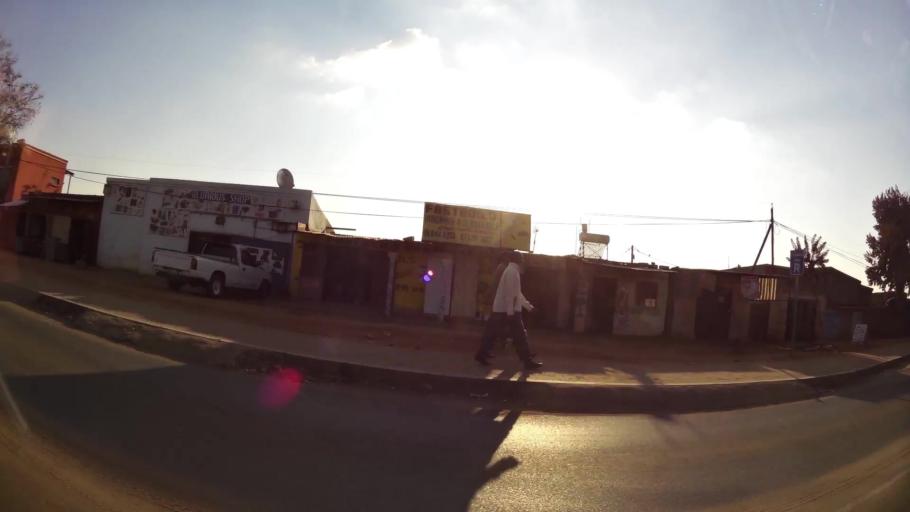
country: ZA
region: Gauteng
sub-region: Ekurhuleni Metropolitan Municipality
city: Tembisa
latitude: -25.9897
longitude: 28.2014
